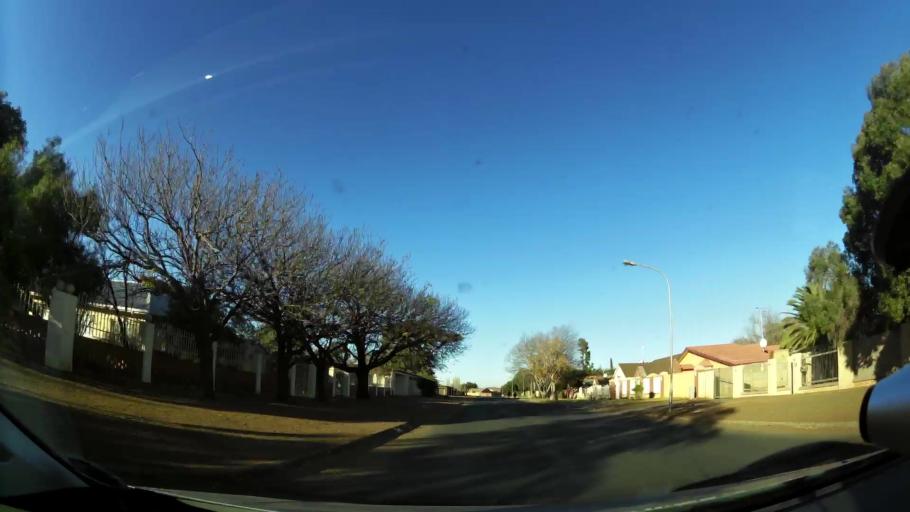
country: ZA
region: Northern Cape
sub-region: Frances Baard District Municipality
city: Kimberley
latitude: -28.7550
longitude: 24.7403
